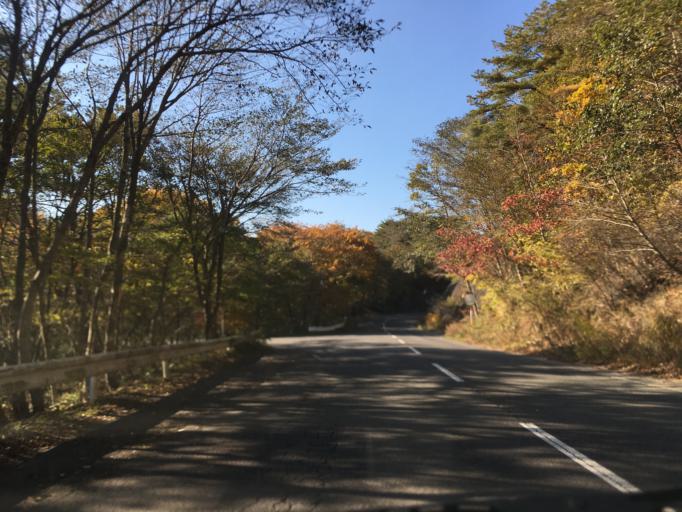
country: JP
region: Fukushima
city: Sukagawa
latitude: 37.2665
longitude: 140.0988
